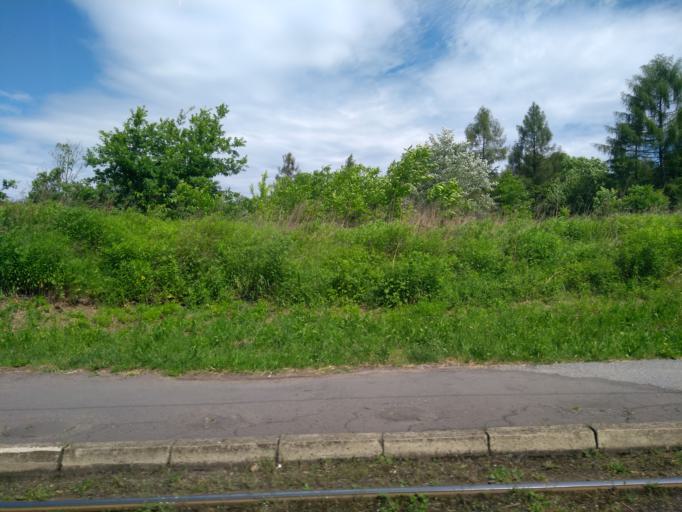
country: PL
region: Lesser Poland Voivodeship
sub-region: Powiat wielicki
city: Kokotow
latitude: 50.0879
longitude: 20.0574
